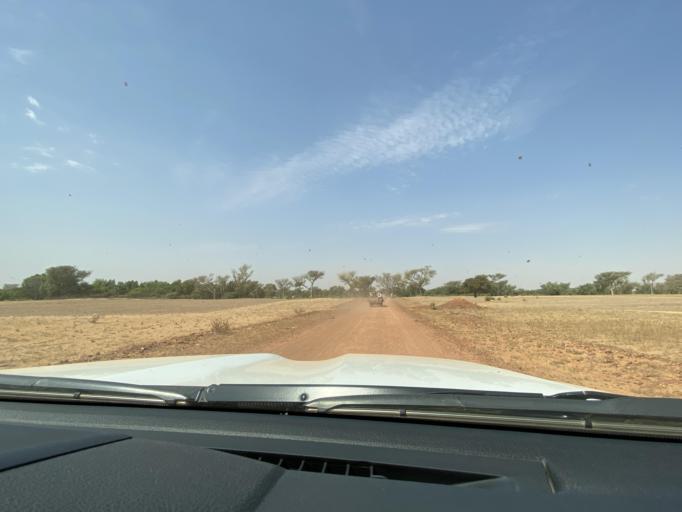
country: NE
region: Dosso
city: Birnin Gaoure
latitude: 13.2455
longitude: 2.8599
